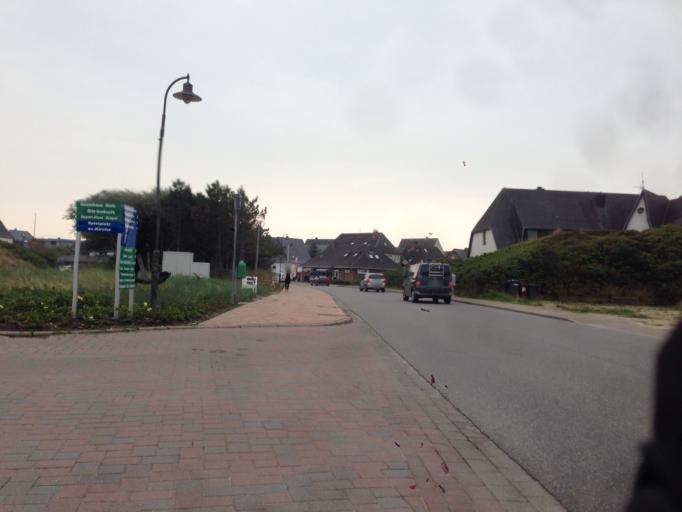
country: DE
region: Schleswig-Holstein
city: Norddorf
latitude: 54.7569
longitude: 8.2866
